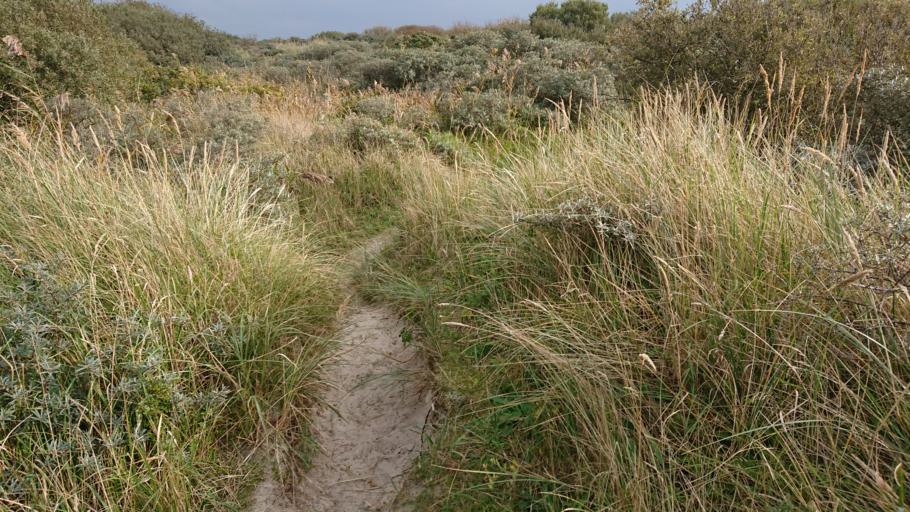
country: DK
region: North Denmark
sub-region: Frederikshavn Kommune
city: Skagen
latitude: 57.7495
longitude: 10.6124
